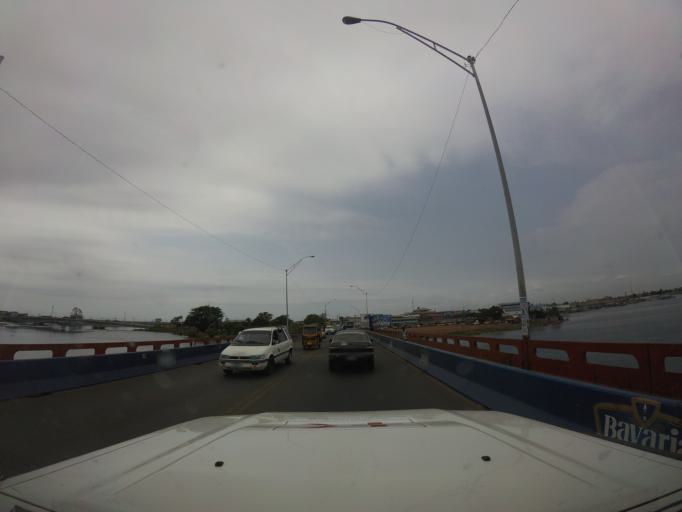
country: LR
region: Montserrado
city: Monrovia
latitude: 6.3207
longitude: -10.8020
